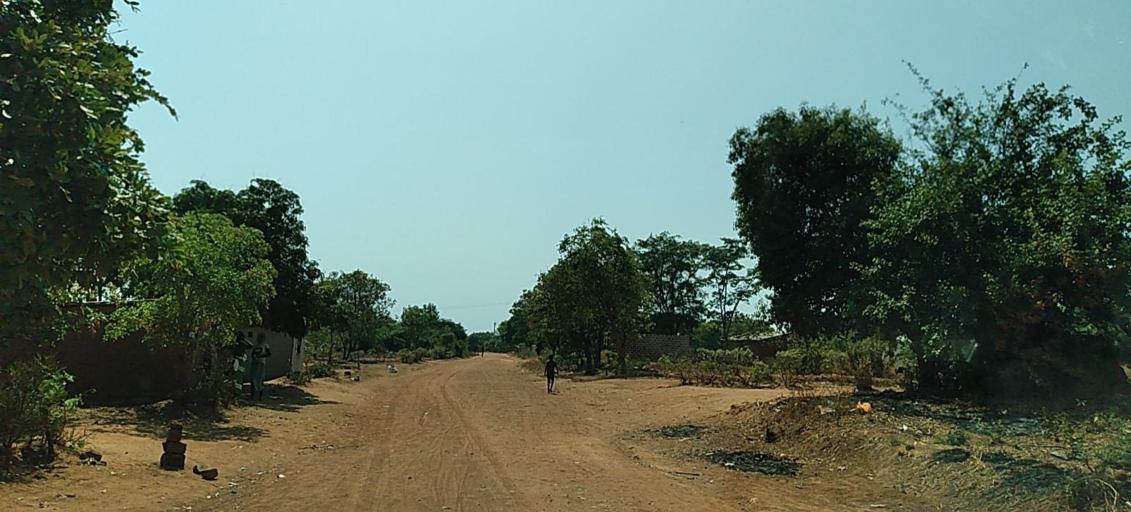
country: ZM
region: Copperbelt
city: Luanshya
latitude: -13.3524
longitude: 28.4099
